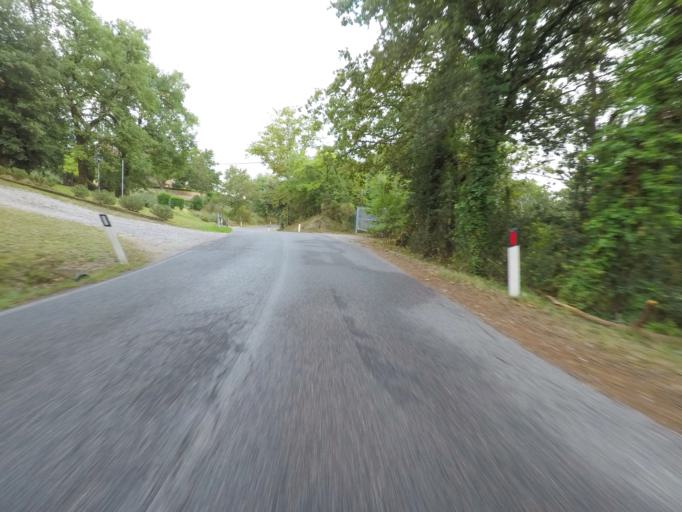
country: IT
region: Tuscany
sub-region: Provincia di Siena
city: Belverde
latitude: 43.3994
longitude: 11.3524
